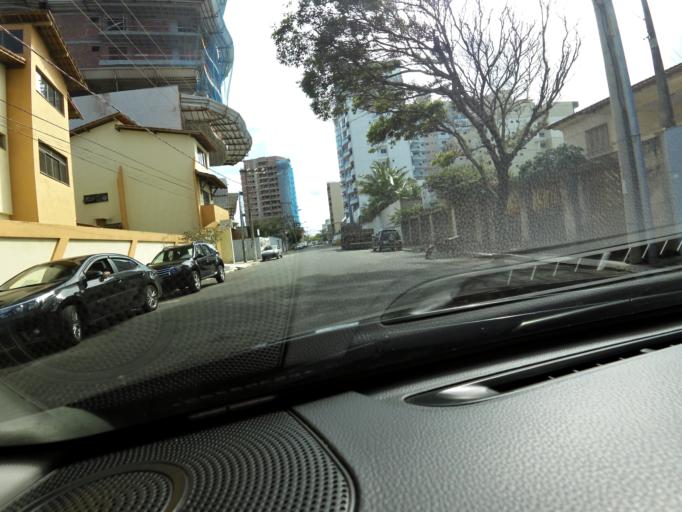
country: BR
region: Espirito Santo
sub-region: Guarapari
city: Guarapari
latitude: -20.6621
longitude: -40.4964
